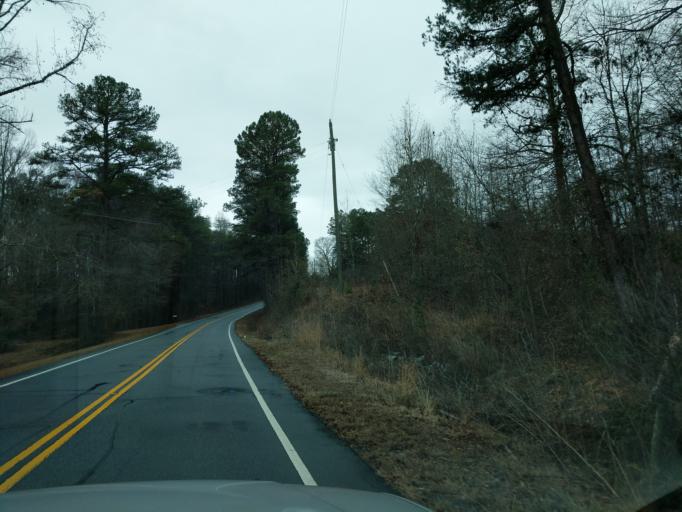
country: US
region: South Carolina
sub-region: Oconee County
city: Walhalla
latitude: 34.7948
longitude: -83.0784
